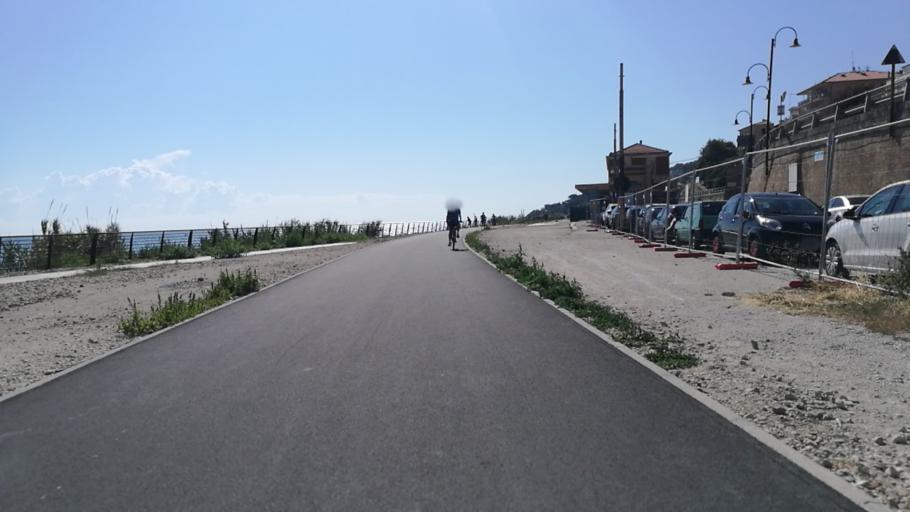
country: IT
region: Abruzzo
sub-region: Provincia di Chieti
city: Marina di San Vito
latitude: 42.3081
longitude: 14.4465
